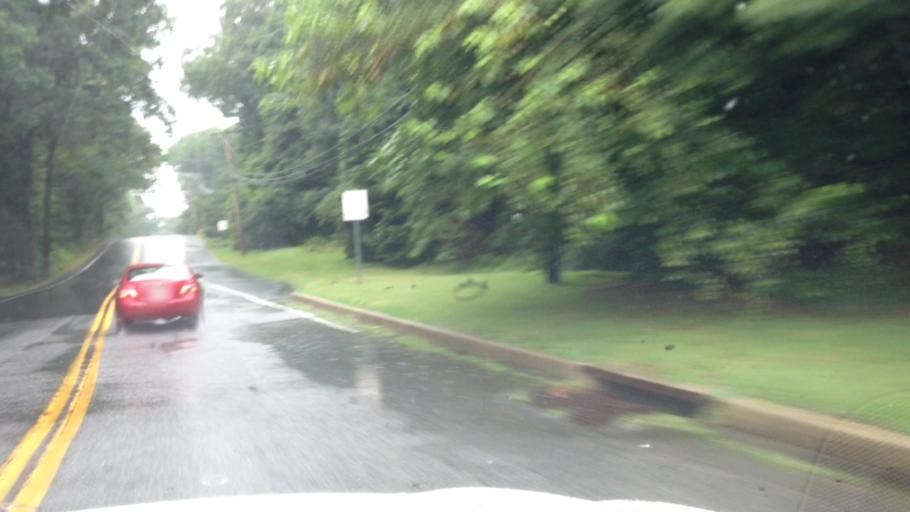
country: US
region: Maryland
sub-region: Anne Arundel County
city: South Gate
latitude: 39.1404
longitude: -76.6534
